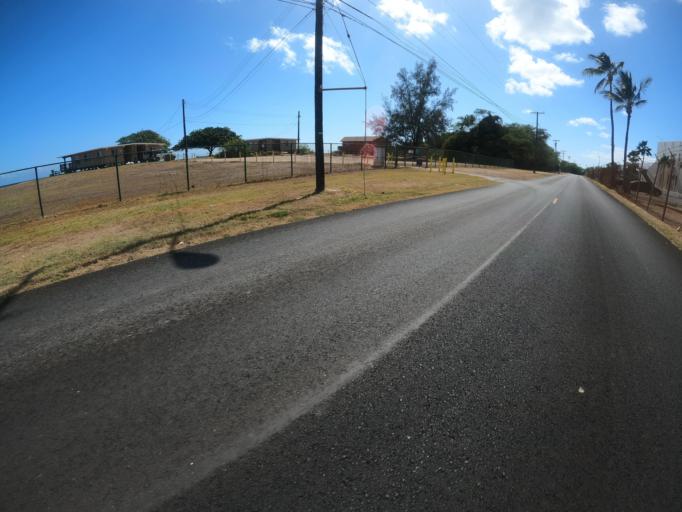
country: US
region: Hawaii
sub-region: Honolulu County
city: Makakilo City
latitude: 21.3002
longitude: -158.0700
